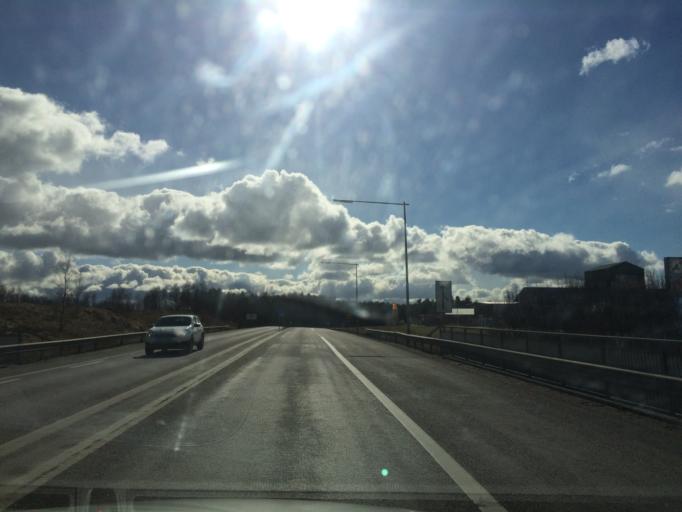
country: SE
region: Vaestra Goetaland
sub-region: Skara Kommun
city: Skara
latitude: 58.3847
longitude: 13.4606
